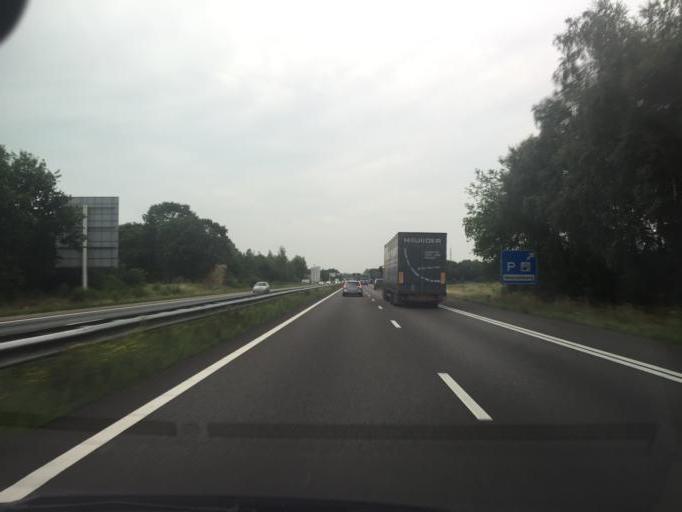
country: NL
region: North Brabant
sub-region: Gemeente Geldrop-Mierlo
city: Geldrop
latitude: 51.4049
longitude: 5.5300
